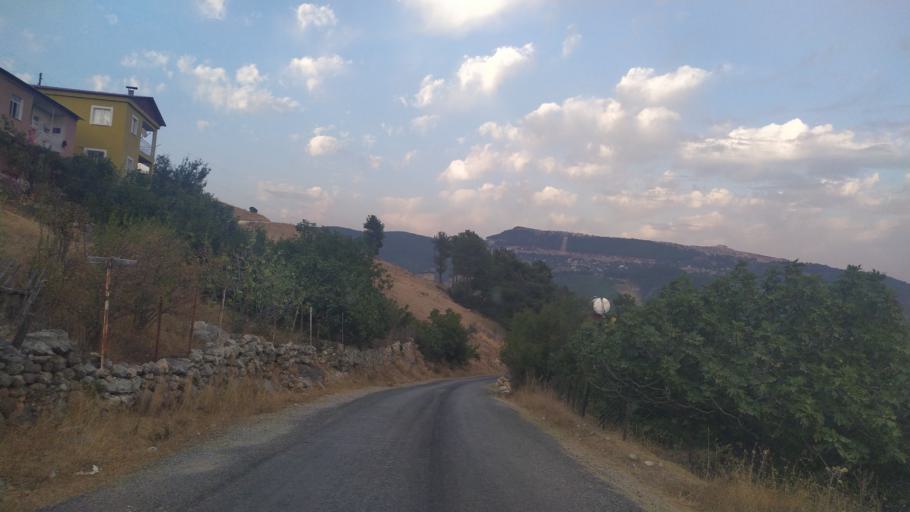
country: TR
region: Mersin
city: Camliyayla
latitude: 37.2306
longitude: 34.7106
